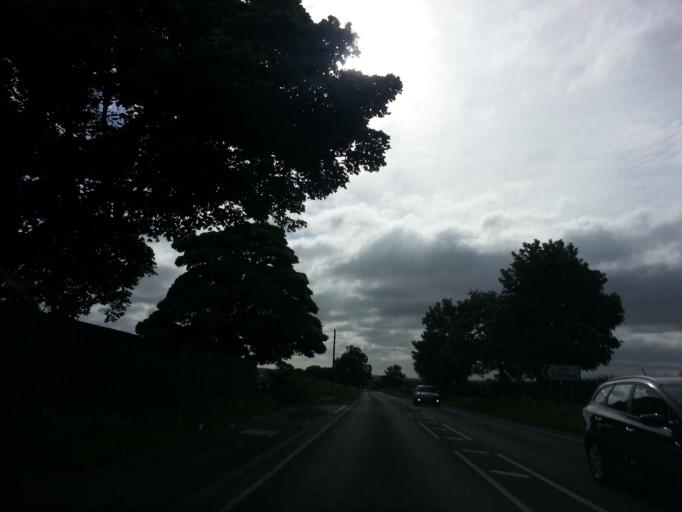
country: GB
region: England
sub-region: County Durham
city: Newton Aycliffe
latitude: 54.6540
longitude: -1.5772
